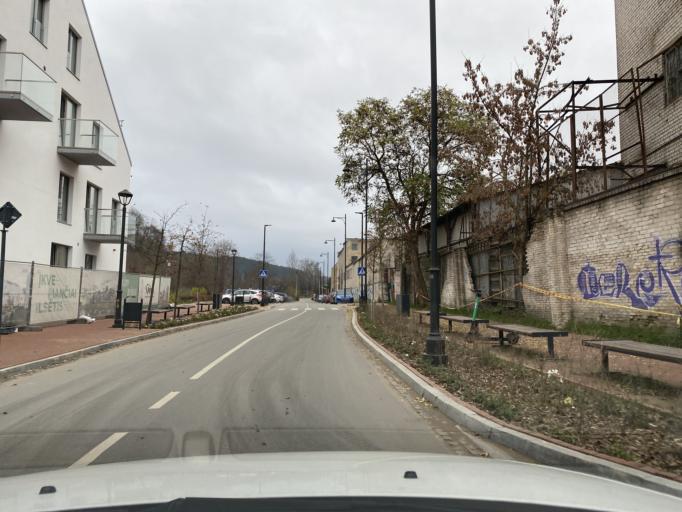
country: LT
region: Vilnius County
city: Rasos
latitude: 54.6791
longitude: 25.3047
